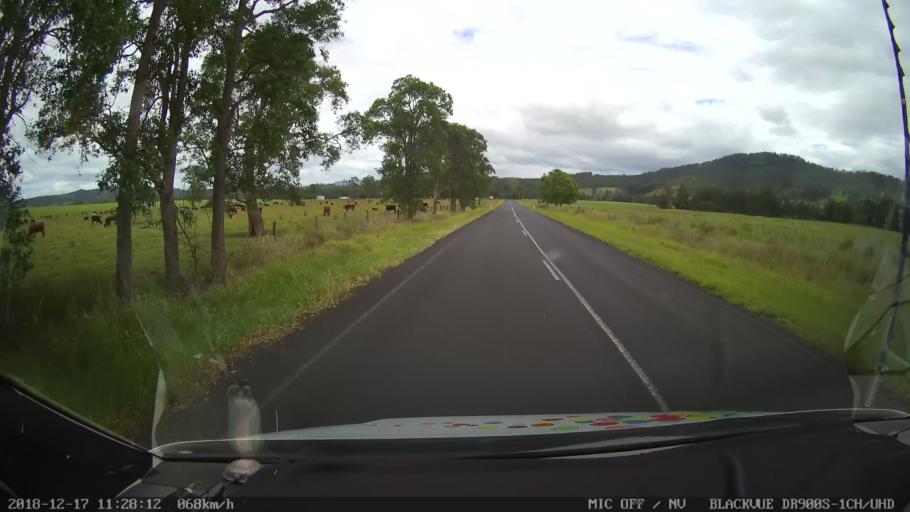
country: AU
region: New South Wales
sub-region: Kyogle
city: Kyogle
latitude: -28.7451
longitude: 152.6389
